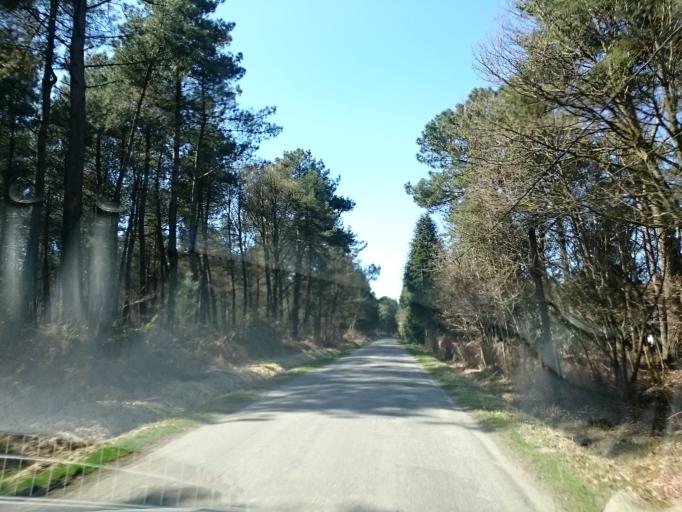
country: FR
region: Brittany
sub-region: Departement d'Ille-et-Vilaine
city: Crevin
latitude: 47.9584
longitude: -1.6678
